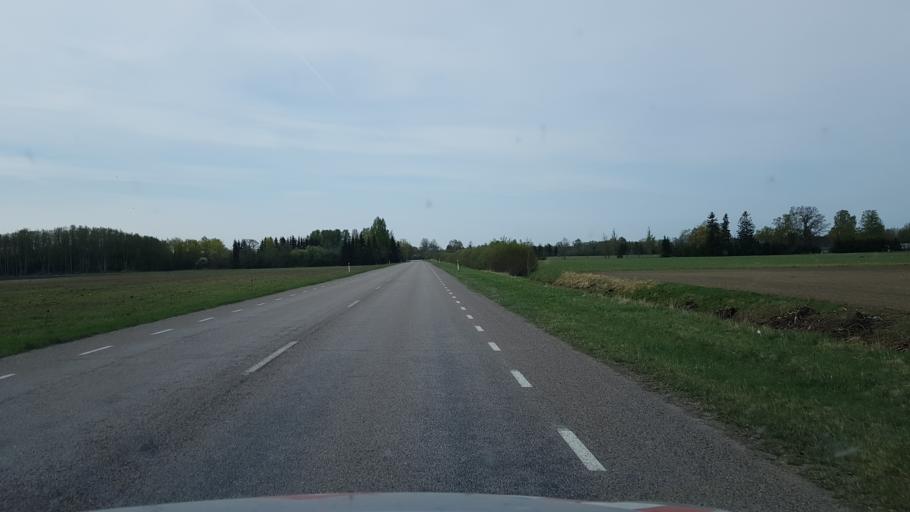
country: EE
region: Paernumaa
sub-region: Audru vald
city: Audru
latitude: 58.3767
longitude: 24.2705
